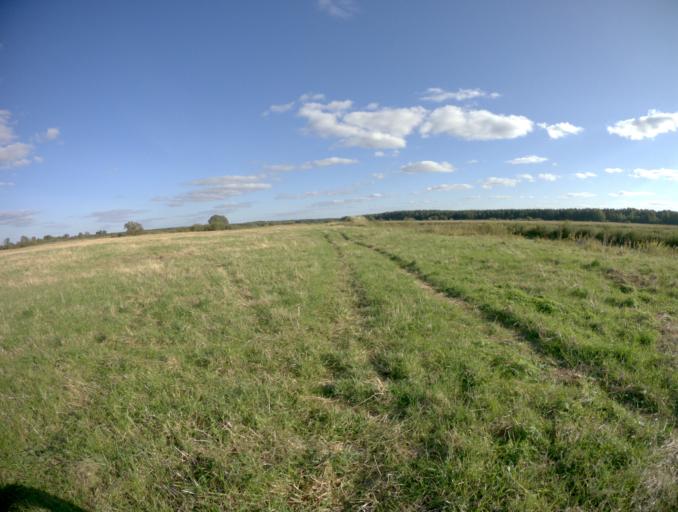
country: RU
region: Vladimir
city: Orgtrud
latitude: 56.3071
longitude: 40.6478
